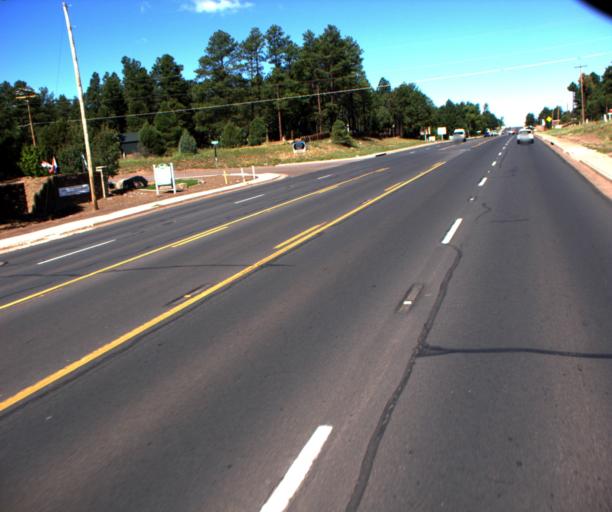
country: US
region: Arizona
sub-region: Navajo County
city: Lake of the Woods
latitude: 34.1605
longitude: -109.9822
